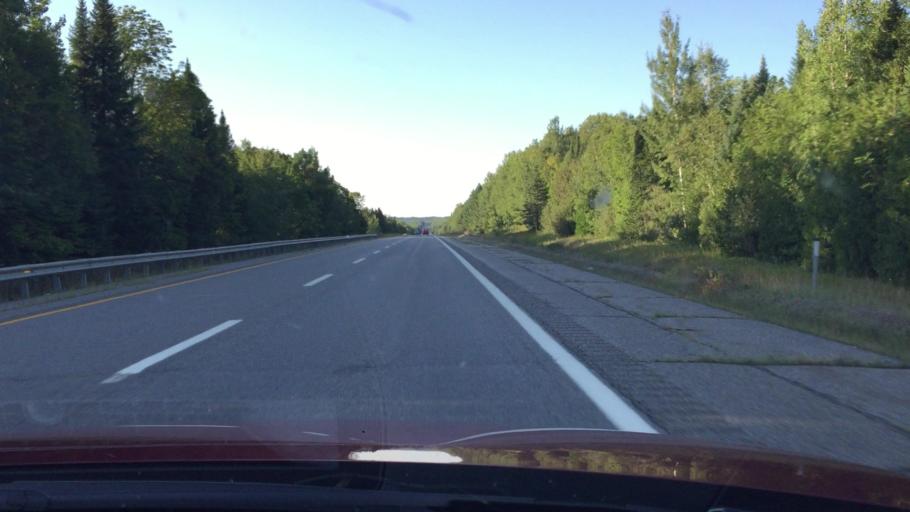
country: US
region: Maine
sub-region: Penobscot County
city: Patten
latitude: 45.8037
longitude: -68.4273
